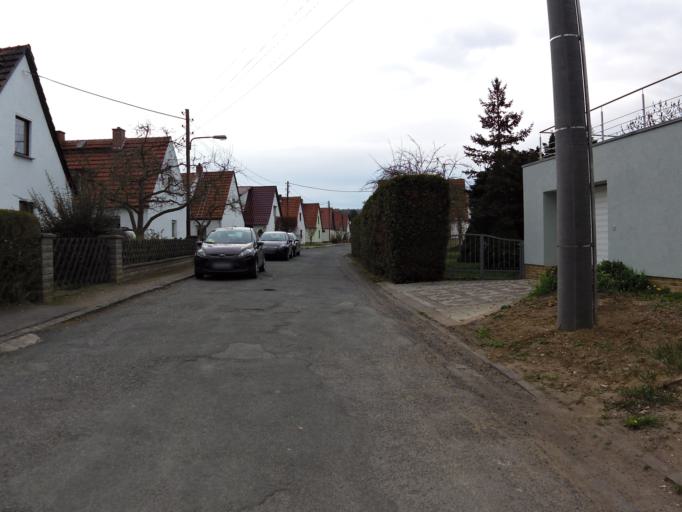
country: DE
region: Thuringia
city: Gotha
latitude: 50.9615
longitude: 10.6948
